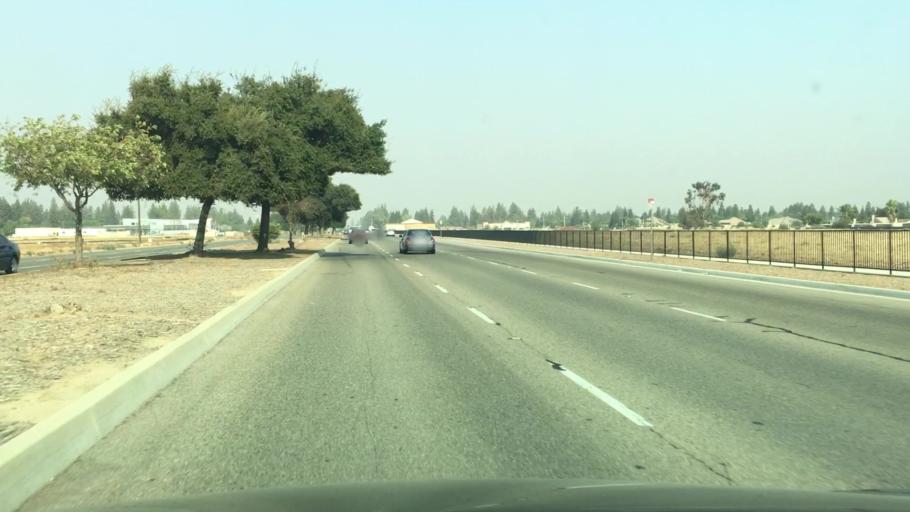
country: US
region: California
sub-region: Fresno County
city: West Park
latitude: 36.8370
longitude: -119.8691
